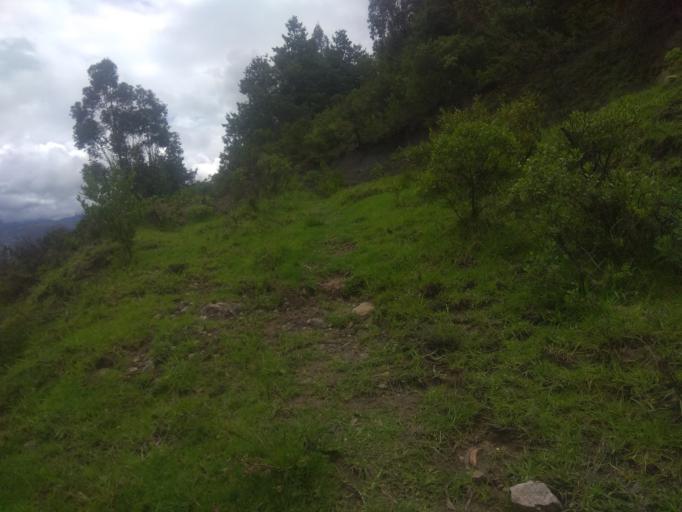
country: CO
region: Boyaca
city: Socota
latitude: 6.0186
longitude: -72.6593
